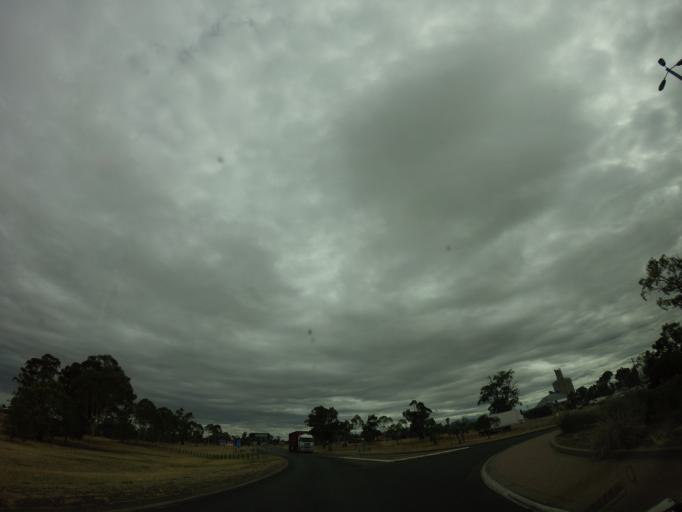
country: AU
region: New South Wales
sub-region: Narrabri
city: Narrabri
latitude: -30.3478
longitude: 149.7598
